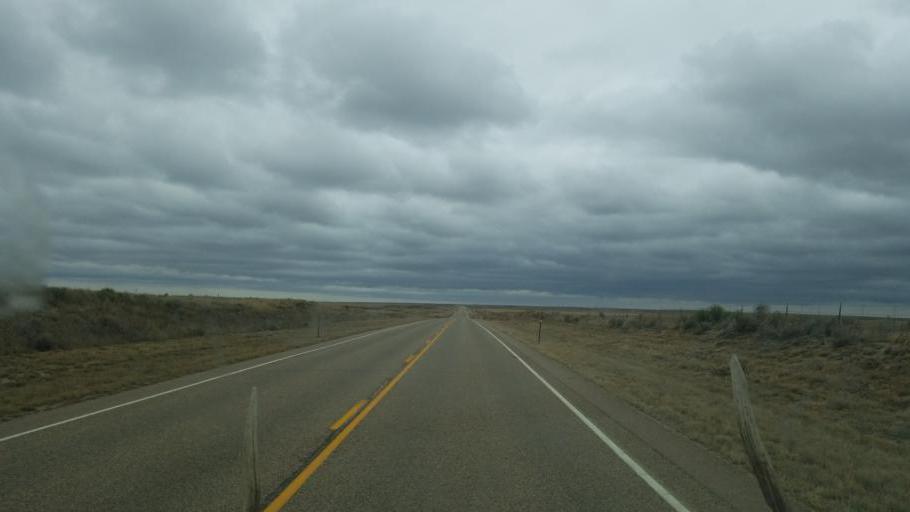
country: US
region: Colorado
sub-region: Kiowa County
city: Eads
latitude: 38.7877
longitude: -102.6862
